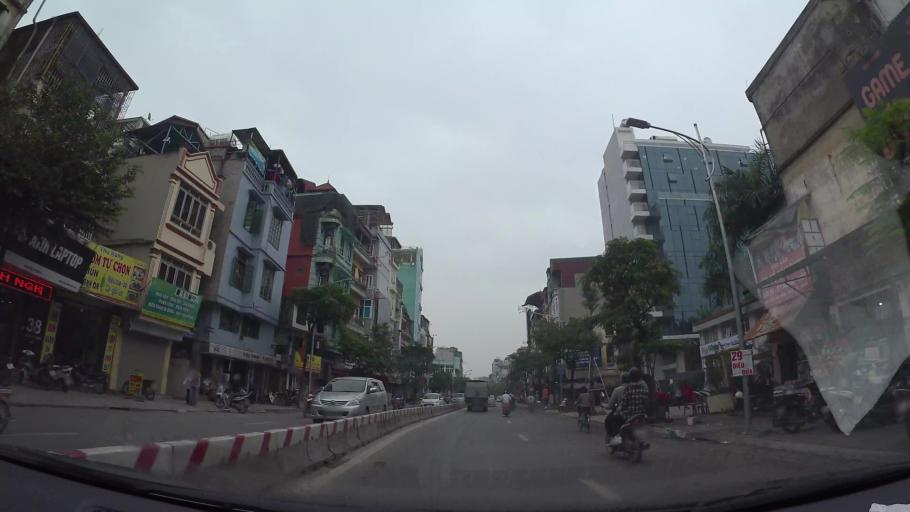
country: VN
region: Ha Noi
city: Hai BaTrung
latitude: 21.0034
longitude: 105.8500
